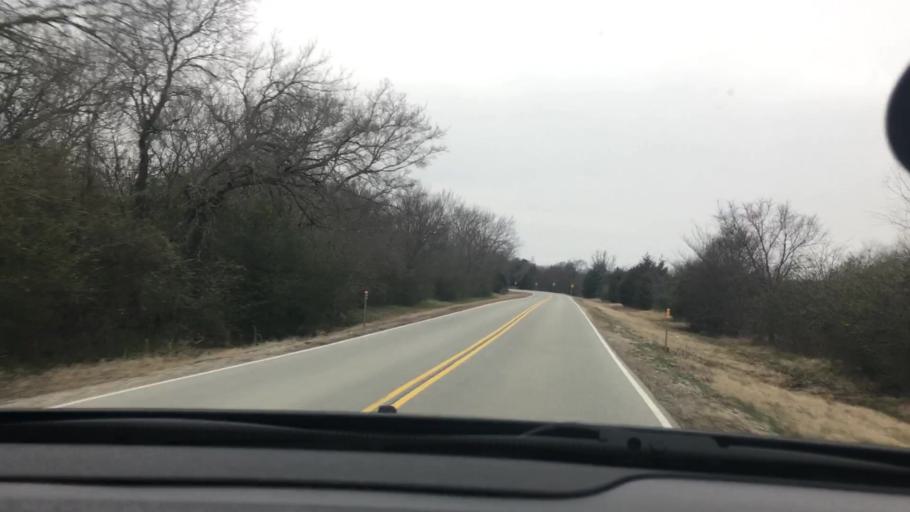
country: US
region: Oklahoma
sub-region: Coal County
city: Coalgate
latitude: 34.5311
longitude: -96.2594
